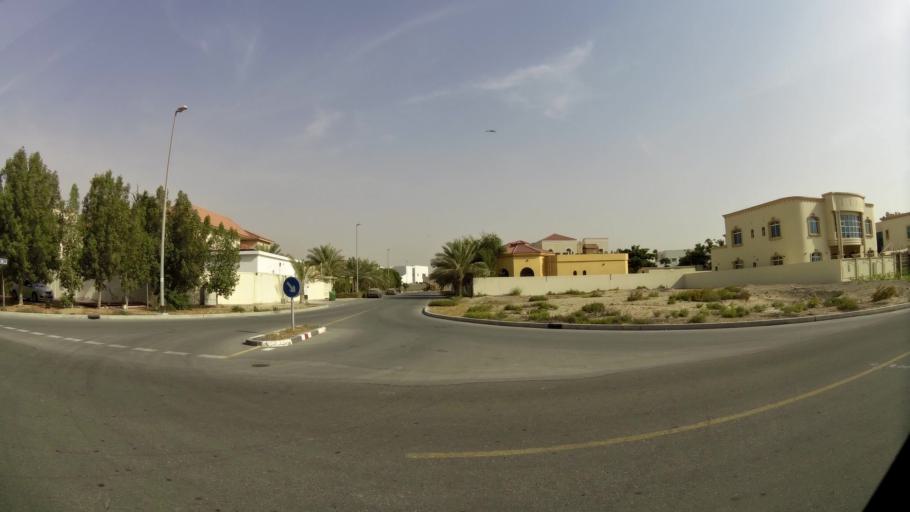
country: AE
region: Ash Shariqah
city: Sharjah
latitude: 25.2502
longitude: 55.4286
